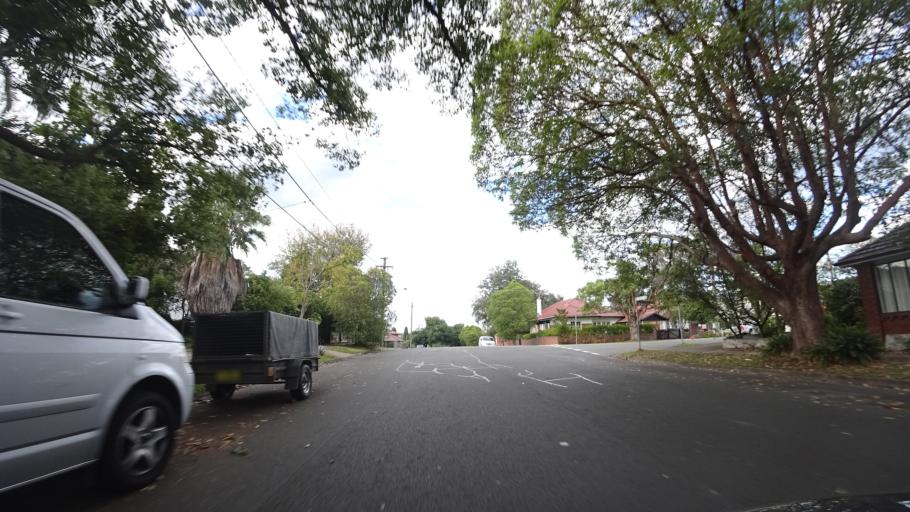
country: AU
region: New South Wales
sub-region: Willoughby
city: Chatswood
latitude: -33.7967
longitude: 151.1926
